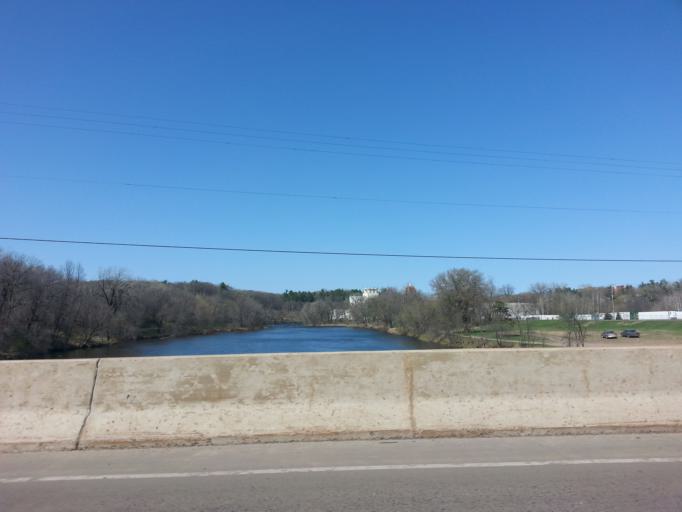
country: US
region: Wisconsin
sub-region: Dunn County
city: Menomonie
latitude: 44.8754
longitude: -91.9379
